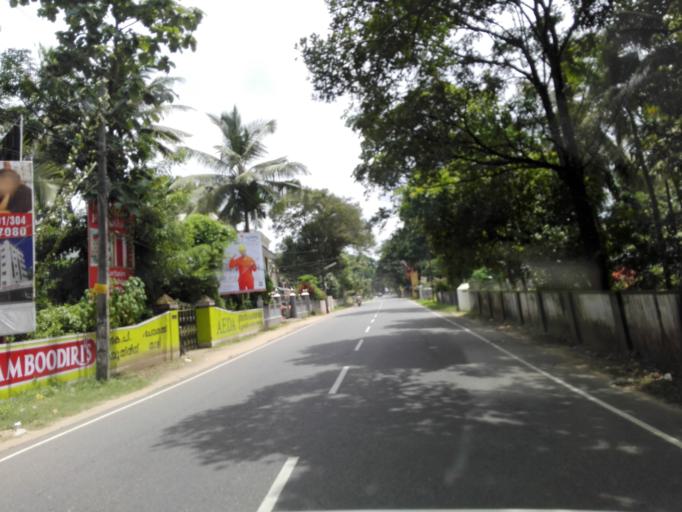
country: IN
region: Kerala
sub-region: Alappuzha
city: Arukutti
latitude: 9.8656
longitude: 76.3817
